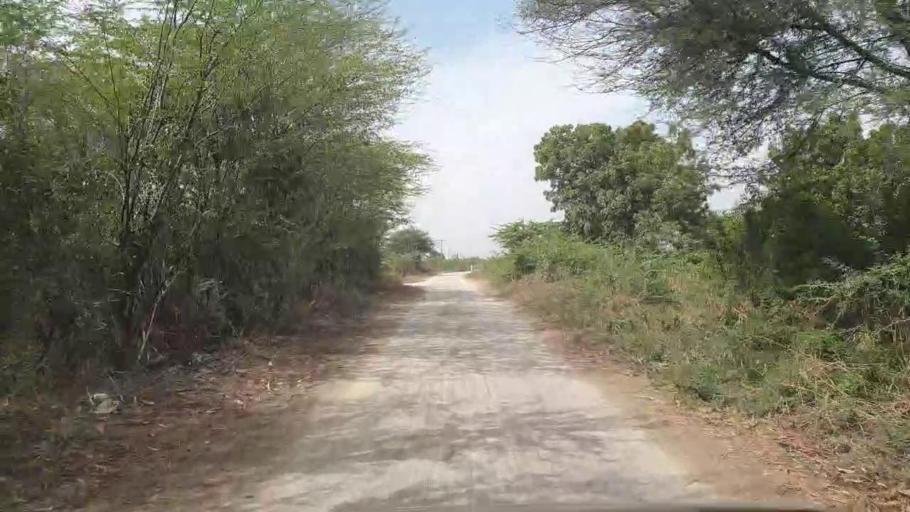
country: PK
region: Sindh
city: Kunri
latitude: 25.2270
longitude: 69.6869
